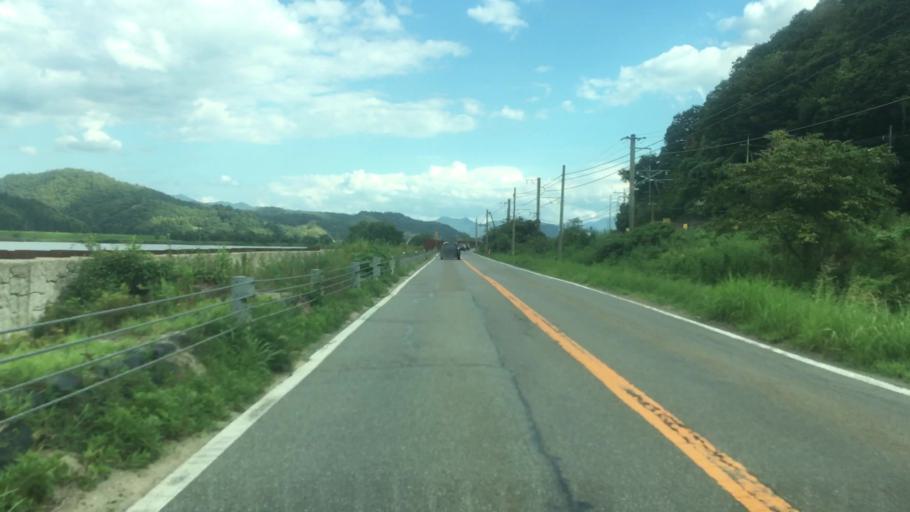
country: JP
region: Hyogo
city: Toyooka
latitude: 35.5769
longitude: 134.8032
